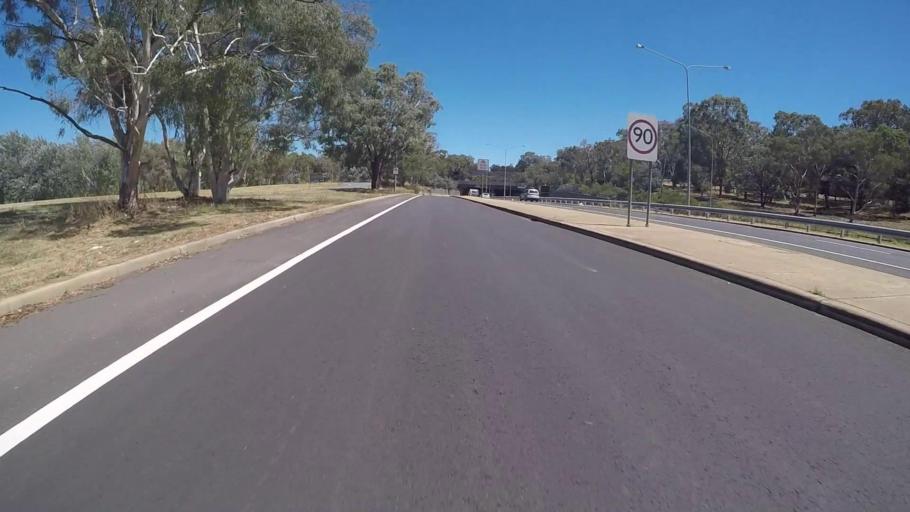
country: AU
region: Australian Capital Territory
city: Canberra
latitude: -35.2863
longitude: 149.1203
